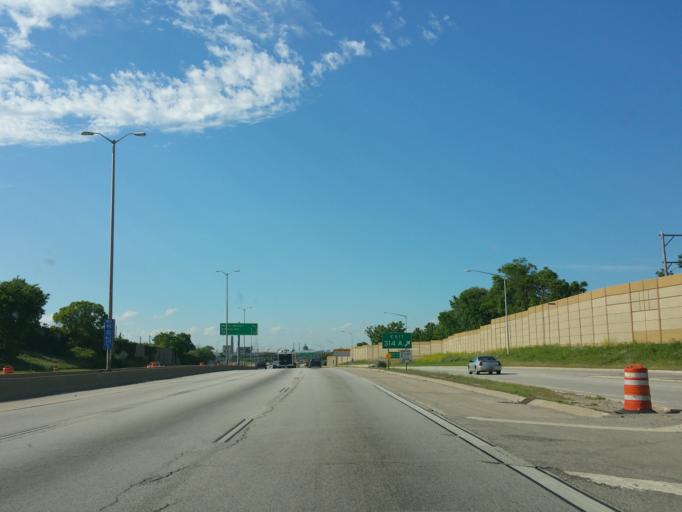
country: US
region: Wisconsin
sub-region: Milwaukee County
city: Saint Francis
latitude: 42.9756
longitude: -87.9154
